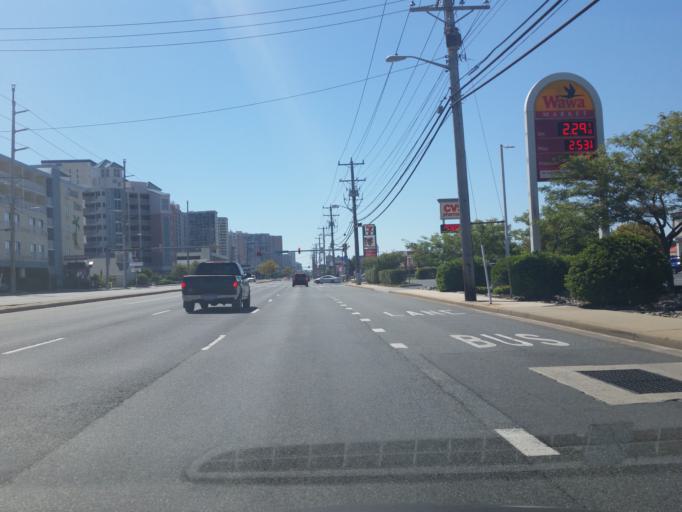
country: US
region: Maryland
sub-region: Worcester County
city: Ocean City
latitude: 38.4265
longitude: -75.0558
